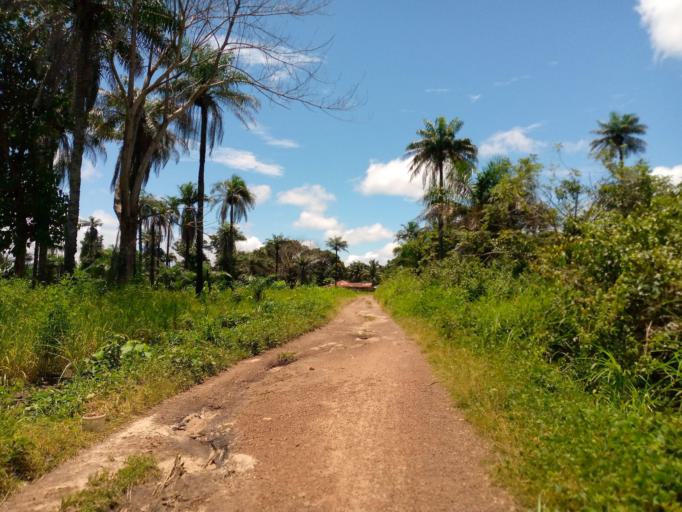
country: SL
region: Northern Province
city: Binkolo
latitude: 9.0579
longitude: -12.1520
